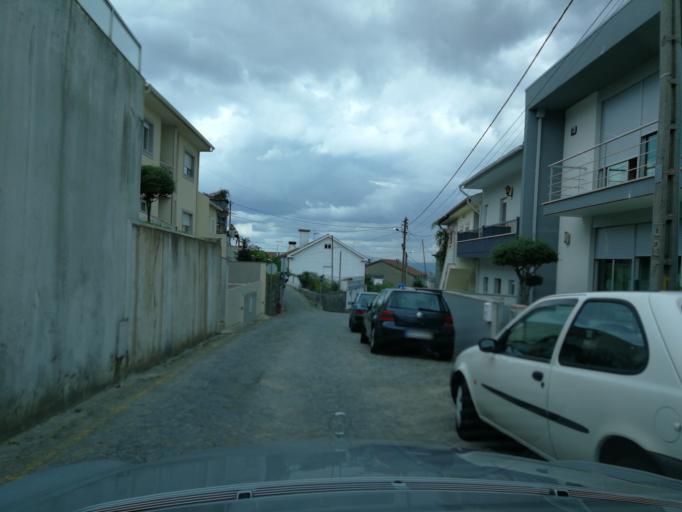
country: PT
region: Braga
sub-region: Braga
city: Braga
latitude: 41.5340
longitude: -8.3982
